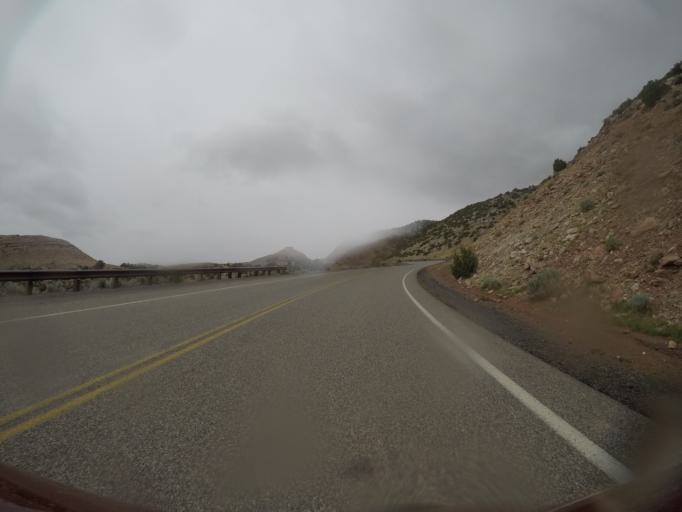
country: US
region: Wyoming
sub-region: Big Horn County
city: Lovell
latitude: 45.0381
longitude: -108.2559
